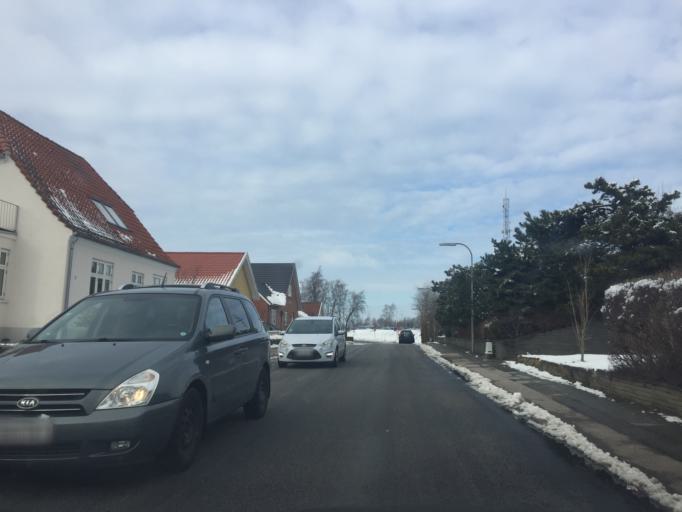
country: DK
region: Capital Region
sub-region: Gribskov Kommune
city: Helsinge
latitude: 56.0225
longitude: 12.1886
